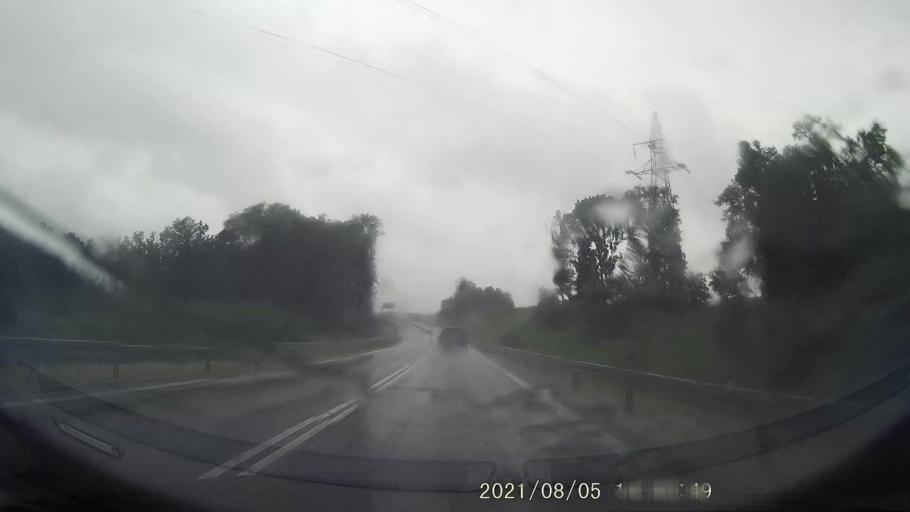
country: PL
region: Opole Voivodeship
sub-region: Powiat nyski
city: Nysa
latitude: 50.4878
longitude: 17.3869
